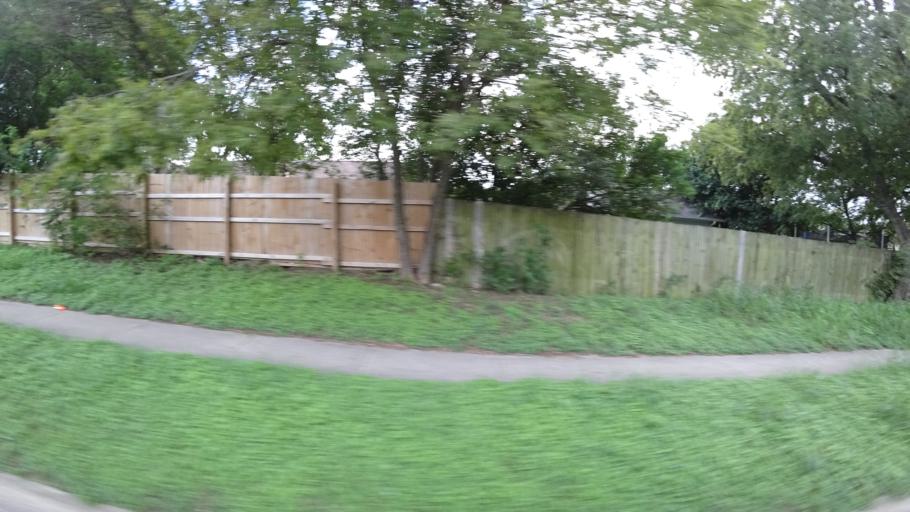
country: US
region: Texas
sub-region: Travis County
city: Onion Creek
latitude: 30.1997
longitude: -97.7973
